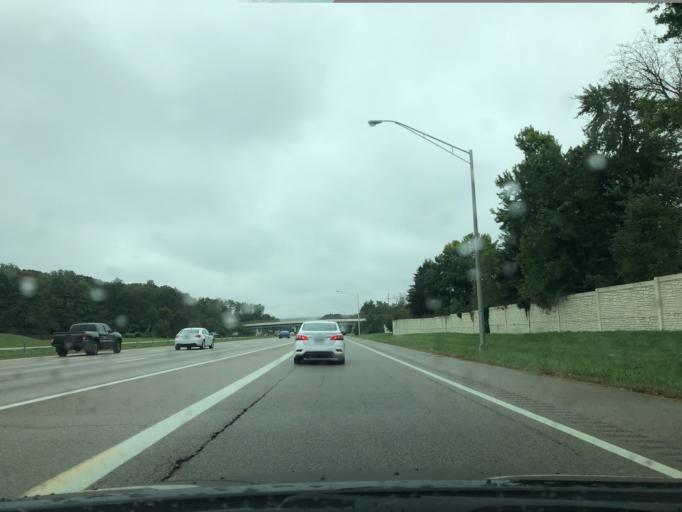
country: US
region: Ohio
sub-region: Hamilton County
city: Sixteen Mile Stand
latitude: 39.2582
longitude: -84.3344
